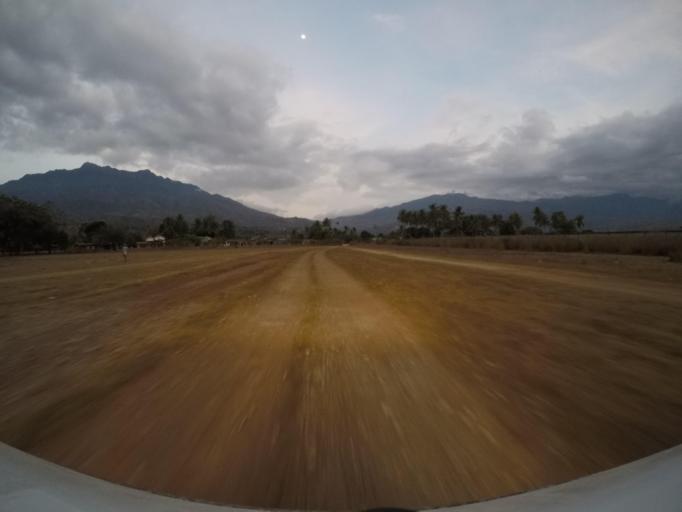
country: TL
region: Bobonaro
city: Maliana
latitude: -8.9738
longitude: 125.2182
